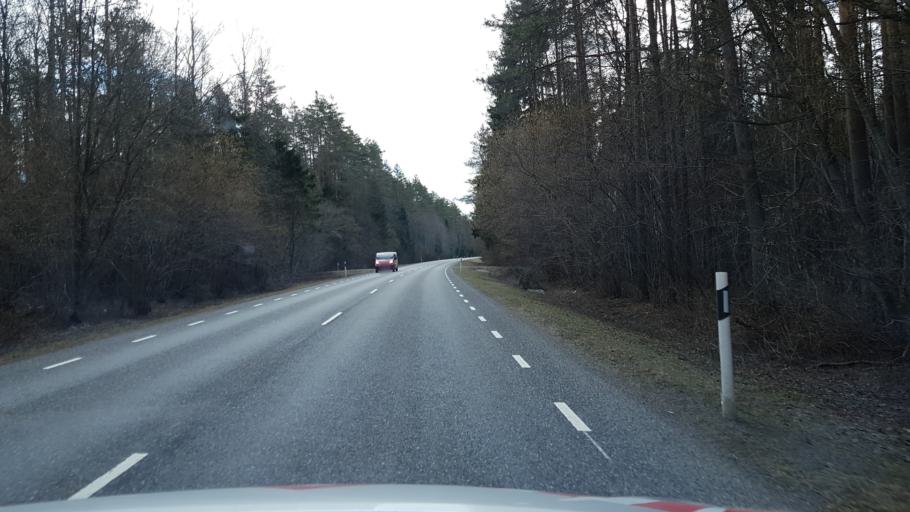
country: EE
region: Laeaene-Virumaa
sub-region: Vaeike-Maarja vald
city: Vaike-Maarja
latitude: 59.0806
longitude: 26.2397
